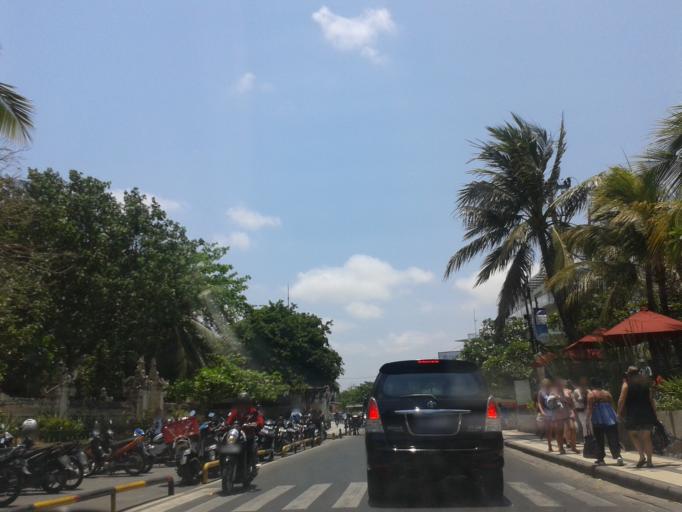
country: ID
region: Bali
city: Kuta
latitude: -8.7192
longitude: 115.1692
